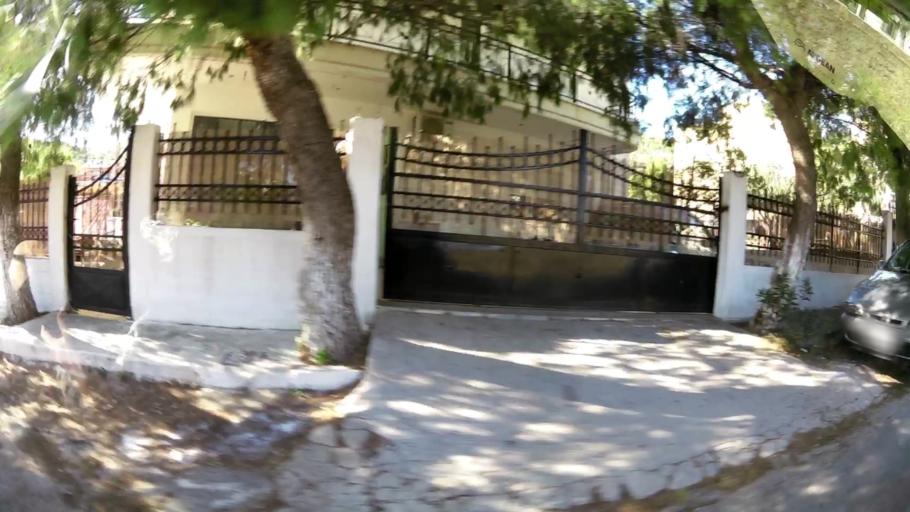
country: GR
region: Attica
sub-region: Nomarchia Anatolikis Attikis
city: Acharnes
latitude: 38.1130
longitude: 23.7227
